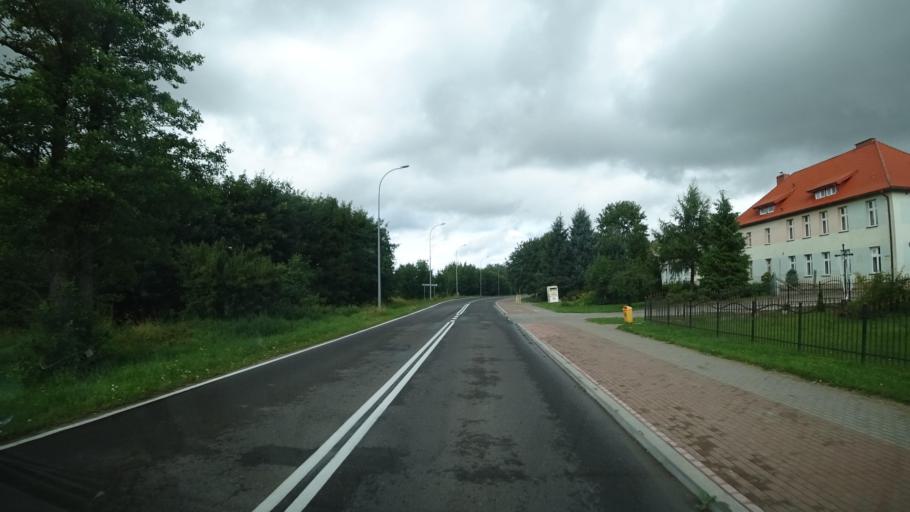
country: PL
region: Warmian-Masurian Voivodeship
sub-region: Powiat olecki
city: Kowale Oleckie
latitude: 54.1695
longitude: 22.4142
